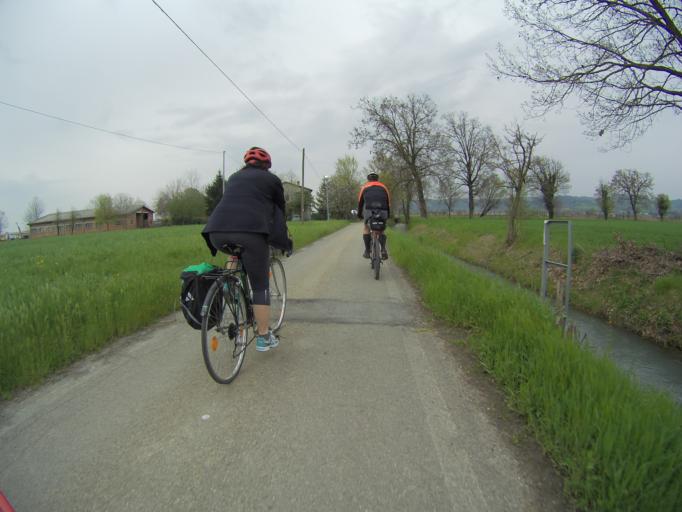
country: IT
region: Emilia-Romagna
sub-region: Provincia di Reggio Emilia
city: San Polo d'Enza
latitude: 44.6521
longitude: 10.4374
